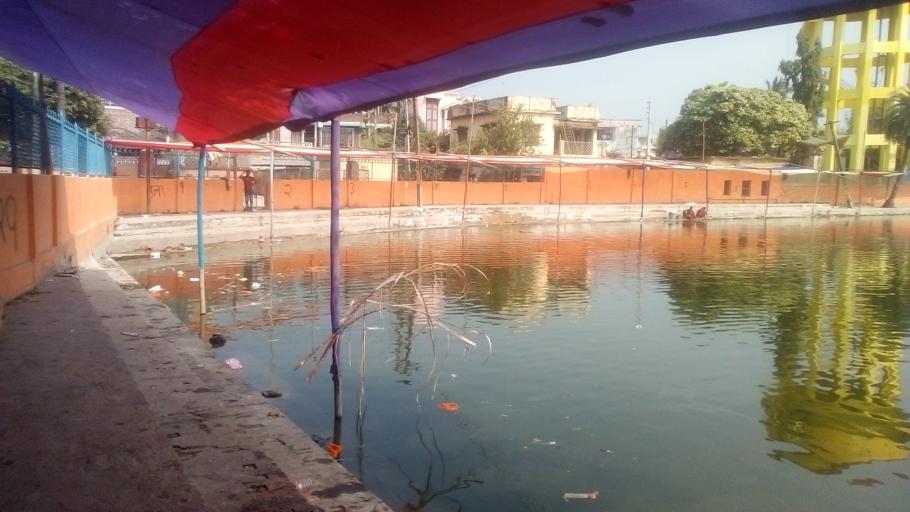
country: NP
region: Central Region
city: Janakpur
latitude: 26.7324
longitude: 85.9247
